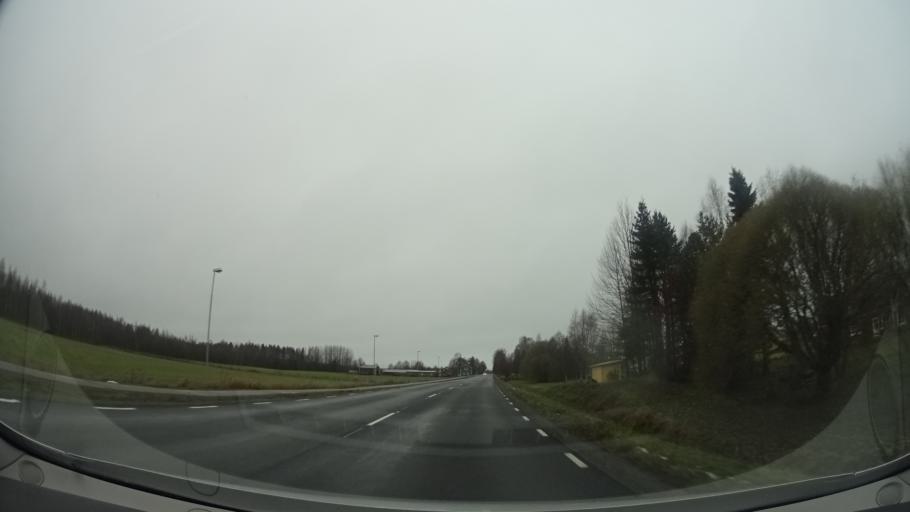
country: SE
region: Vaesterbotten
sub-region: Skelleftea Kommun
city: Kage
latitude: 64.8377
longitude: 20.9677
